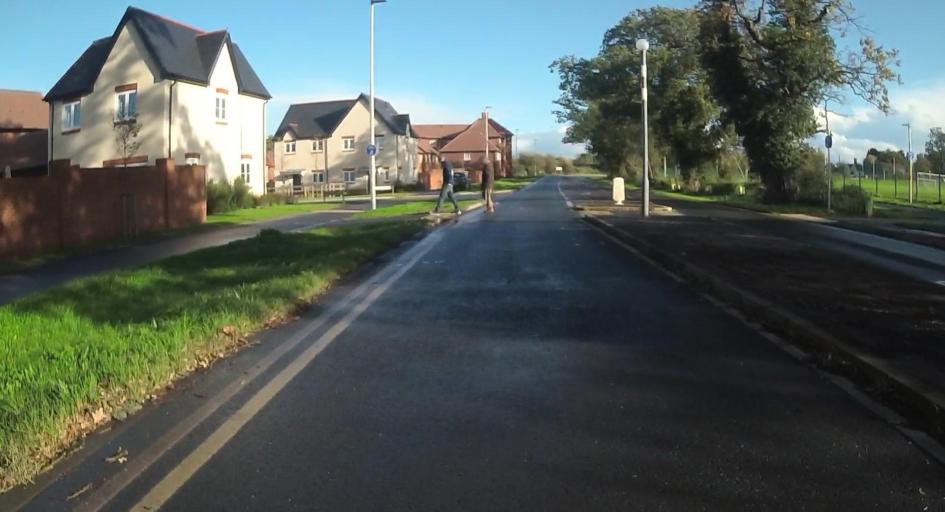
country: GB
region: England
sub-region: Wokingham
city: Wokingham
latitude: 51.4232
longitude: -0.8360
